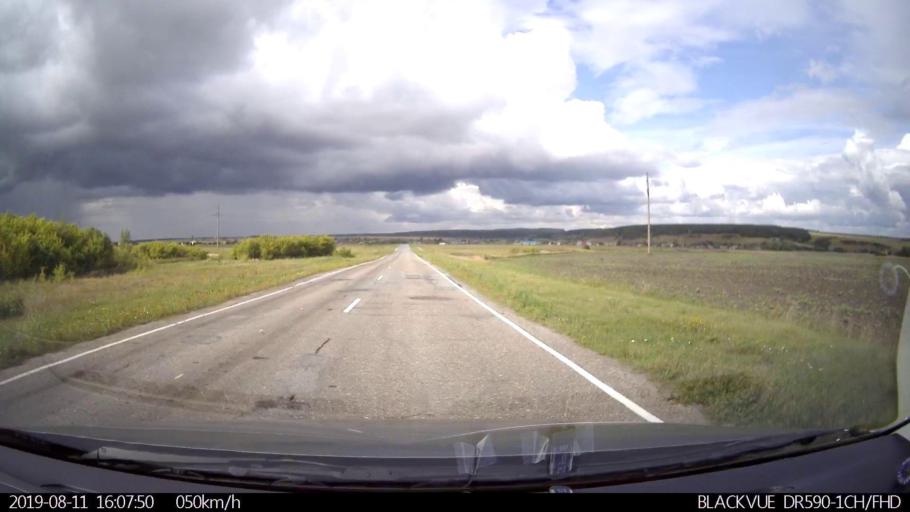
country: RU
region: Ulyanovsk
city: Ignatovka
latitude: 53.9802
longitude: 47.6468
